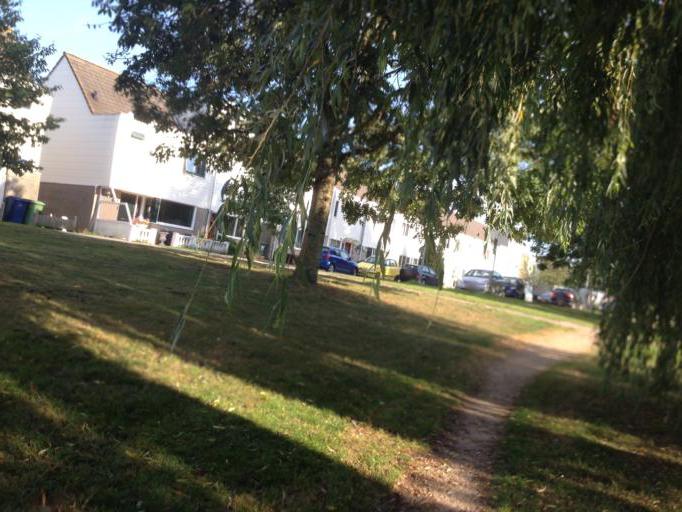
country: NL
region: Flevoland
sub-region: Gemeente Almere
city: Almere Stad
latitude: 52.3947
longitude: 5.2582
